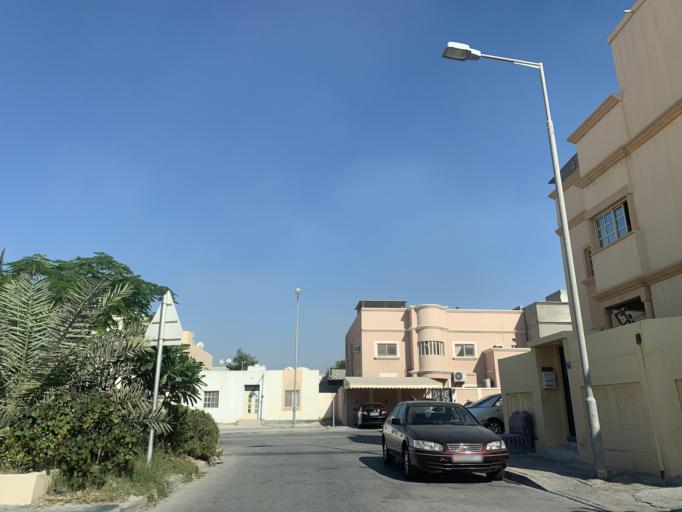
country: BH
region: Central Governorate
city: Madinat Hamad
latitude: 26.1129
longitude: 50.5059
